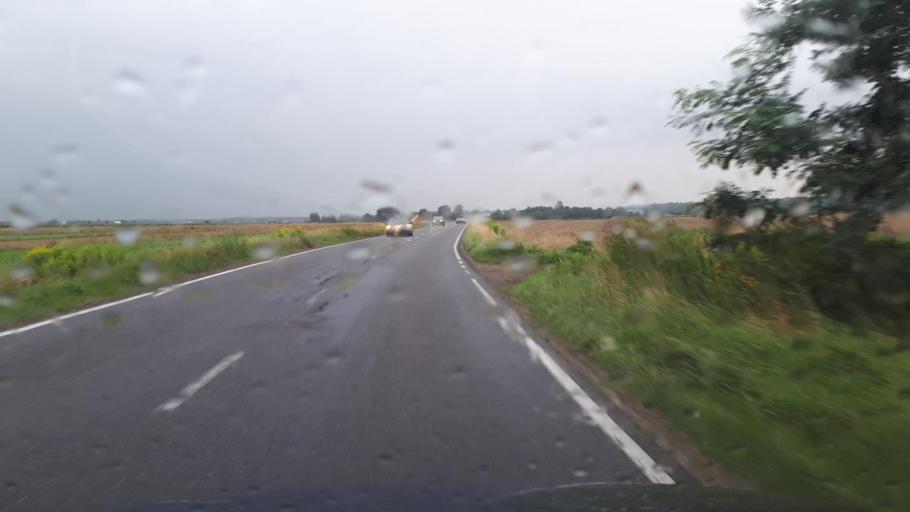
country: PL
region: Silesian Voivodeship
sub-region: Powiat tarnogorski
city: Wieszowa
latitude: 50.3635
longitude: 18.7183
